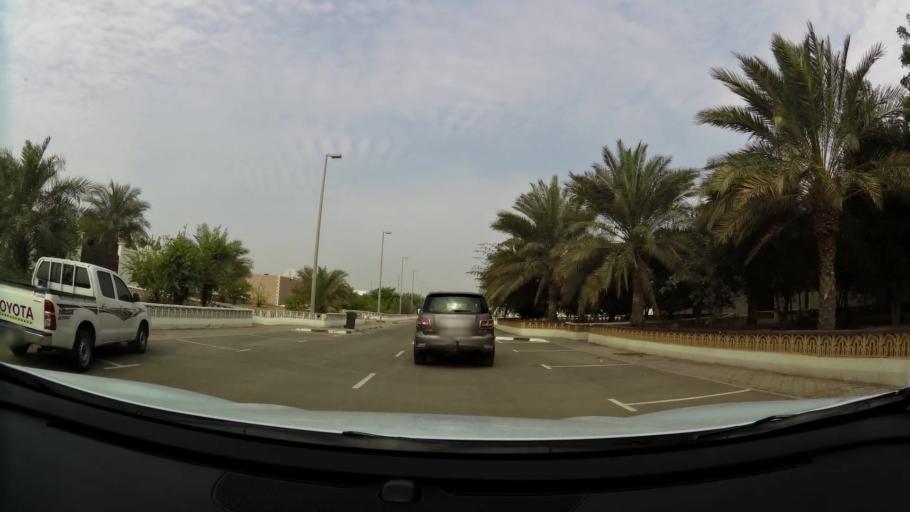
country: AE
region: Abu Dhabi
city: Abu Dhabi
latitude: 24.6786
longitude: 54.7587
